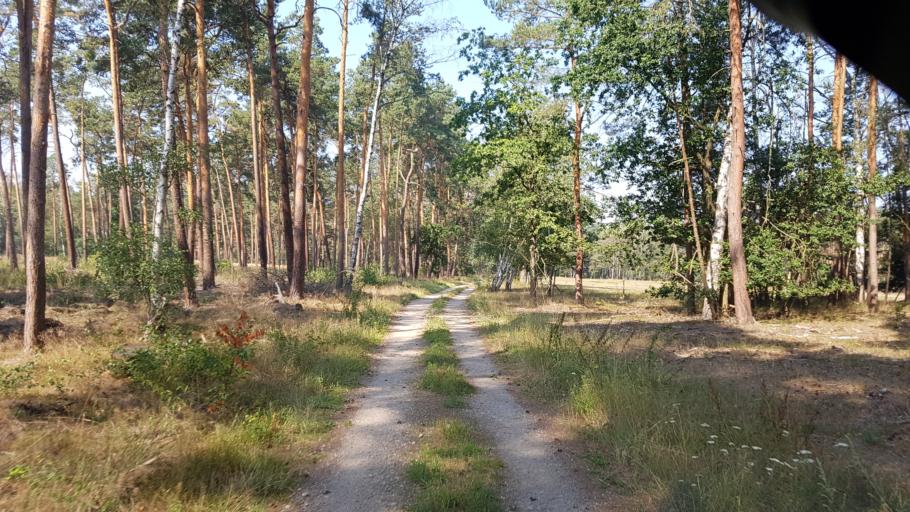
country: DE
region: Brandenburg
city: Cottbus
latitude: 51.7047
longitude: 14.4226
